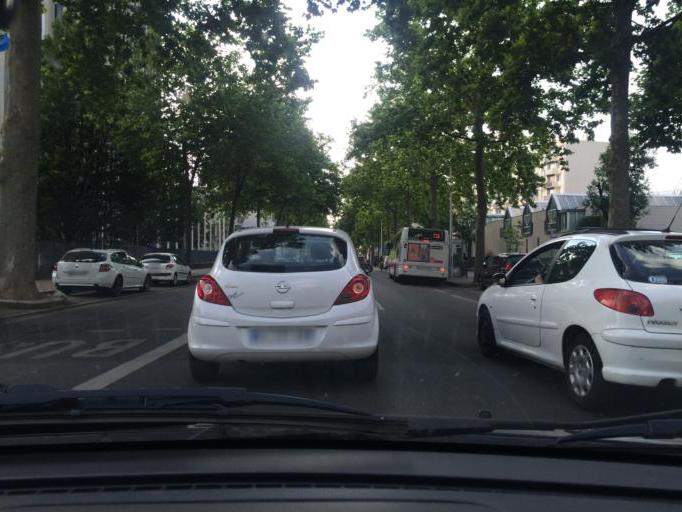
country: FR
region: Rhone-Alpes
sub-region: Departement du Rhone
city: Villeurbanne
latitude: 45.7436
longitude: 4.8771
